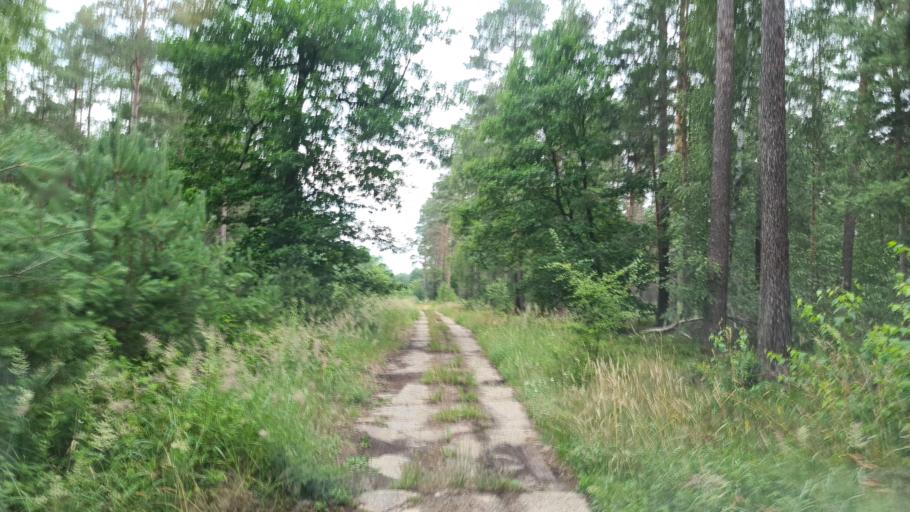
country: DE
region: Brandenburg
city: Crinitz
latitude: 51.7196
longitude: 13.7283
